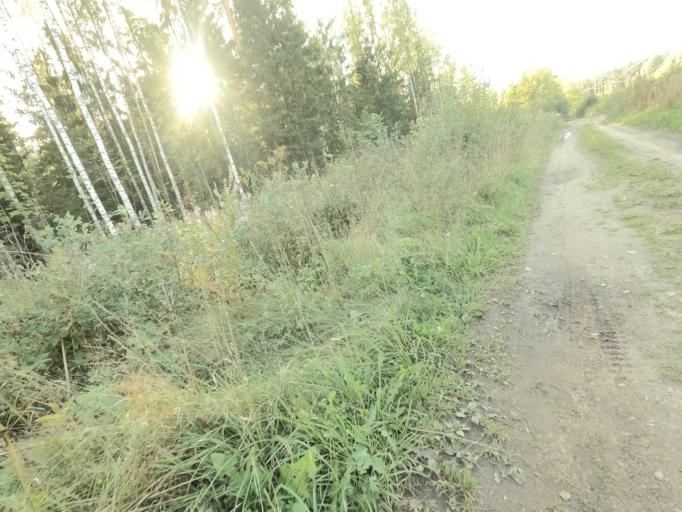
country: RU
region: Leningrad
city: Imeni Sverdlova
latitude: 59.8383
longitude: 30.7315
